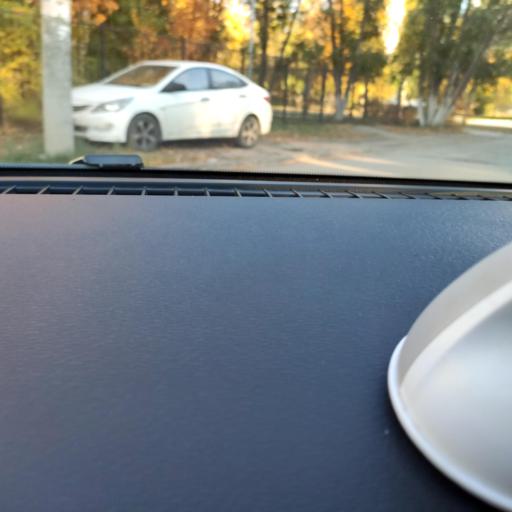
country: RU
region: Samara
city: Samara
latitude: 53.2623
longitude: 50.2296
